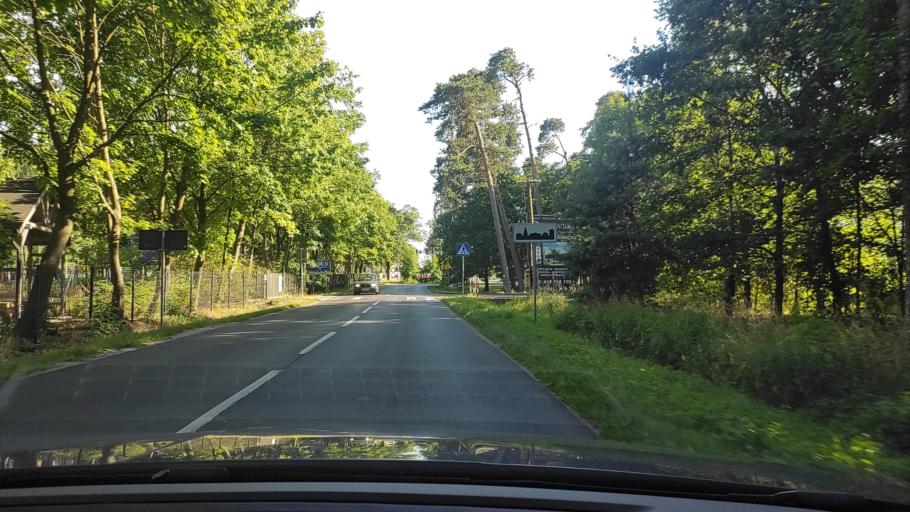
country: PL
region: Greater Poland Voivodeship
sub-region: Powiat poznanski
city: Kobylnica
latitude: 52.4476
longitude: 17.0770
